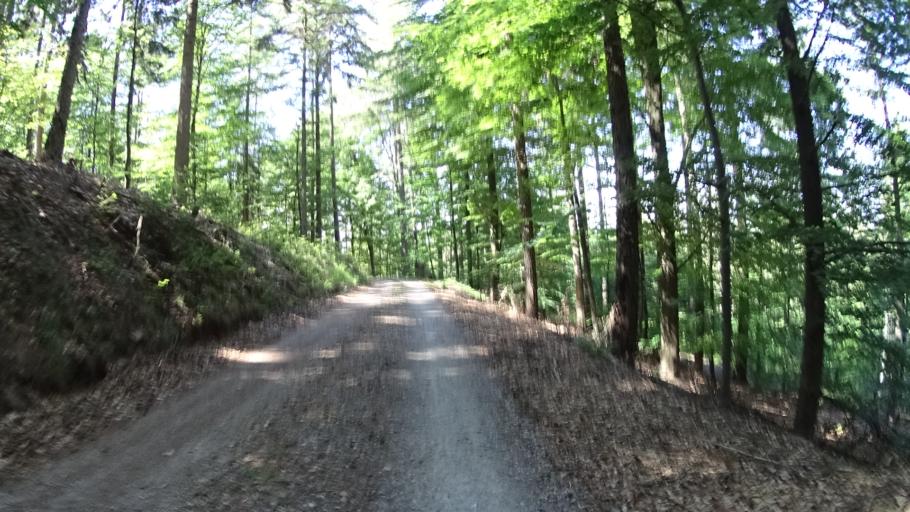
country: DE
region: Baden-Wuerttemberg
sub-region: Karlsruhe Region
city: Dossenheim
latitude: 49.4629
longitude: 8.7126
